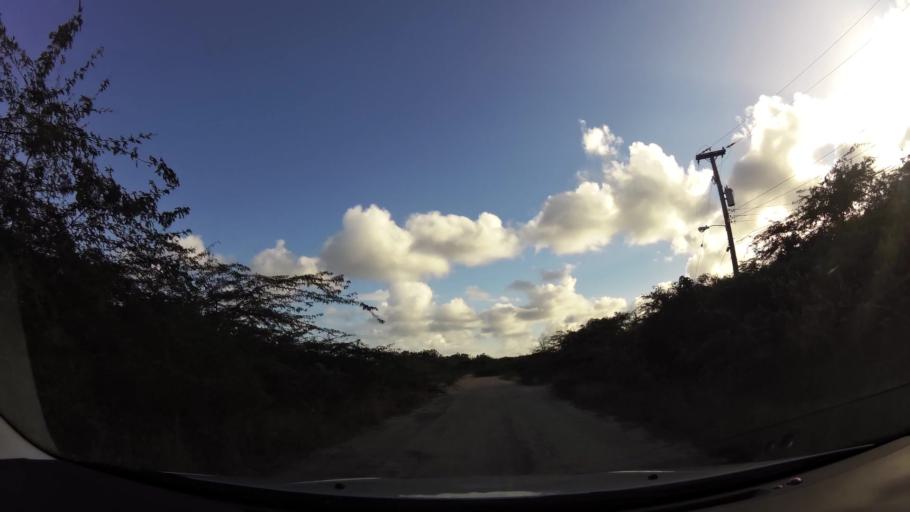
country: AG
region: Saint George
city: Piggotts
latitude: 17.1225
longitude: -61.7877
